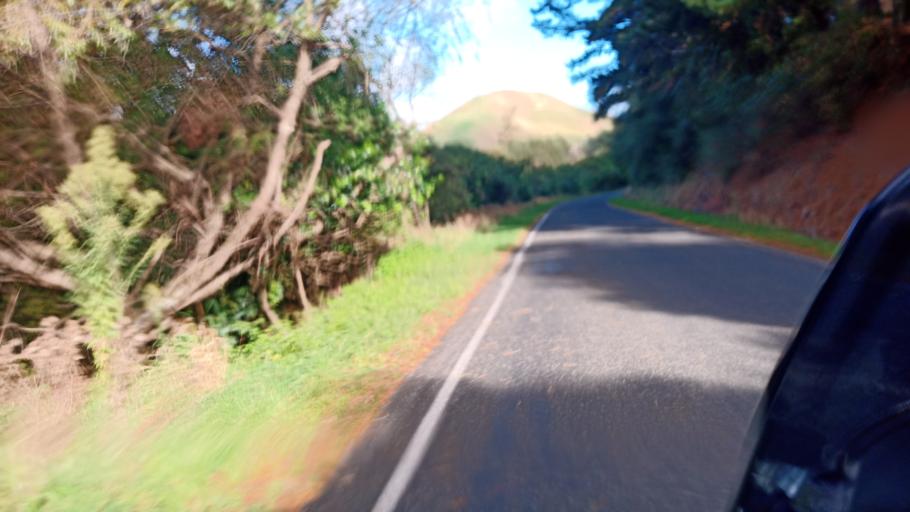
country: NZ
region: Gisborne
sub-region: Gisborne District
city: Gisborne
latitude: -38.5401
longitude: 177.5666
